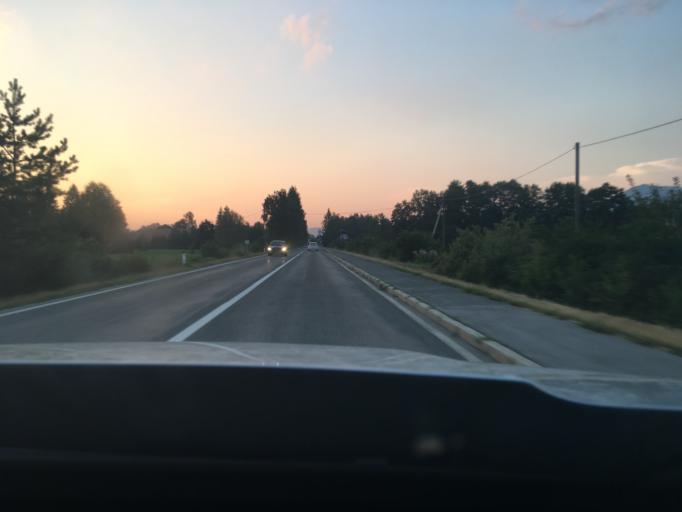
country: SI
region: Ribnica
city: Ribnica
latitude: 45.7248
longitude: 14.7403
